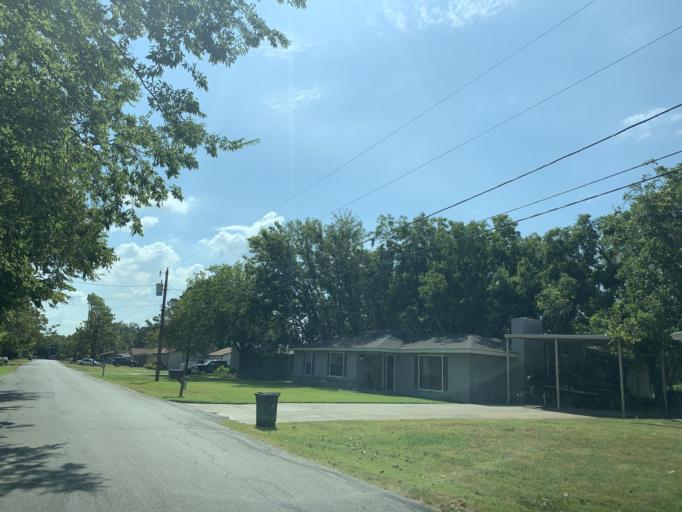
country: US
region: Texas
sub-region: Tarrant County
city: Azle
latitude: 32.8803
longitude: -97.5400
